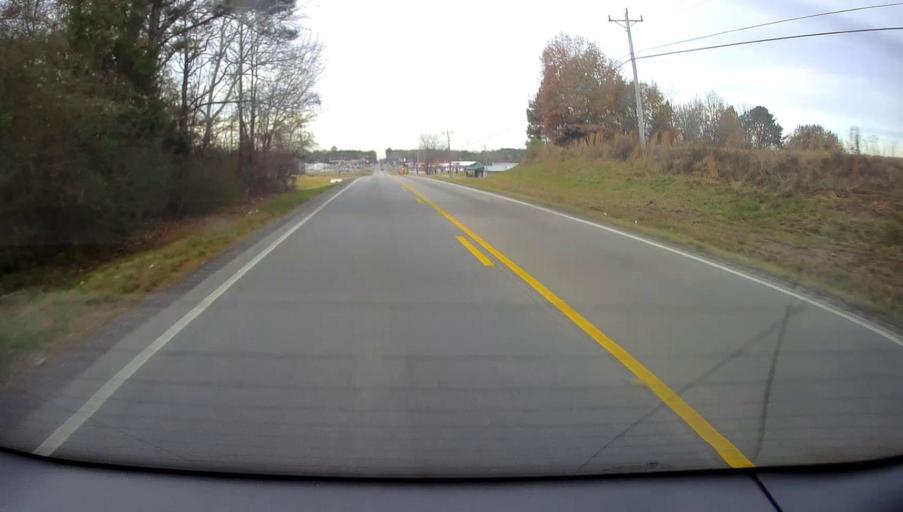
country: US
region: Alabama
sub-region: Morgan County
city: Priceville
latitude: 34.4432
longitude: -86.7518
